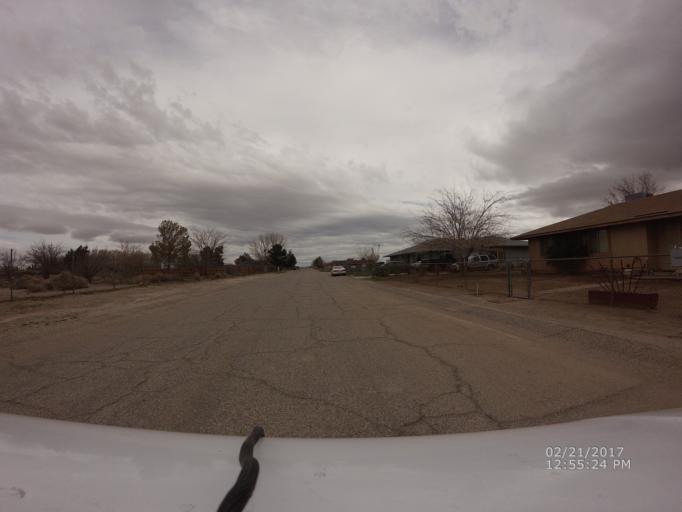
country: US
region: California
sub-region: Los Angeles County
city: Lake Los Angeles
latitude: 34.6399
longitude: -117.8511
